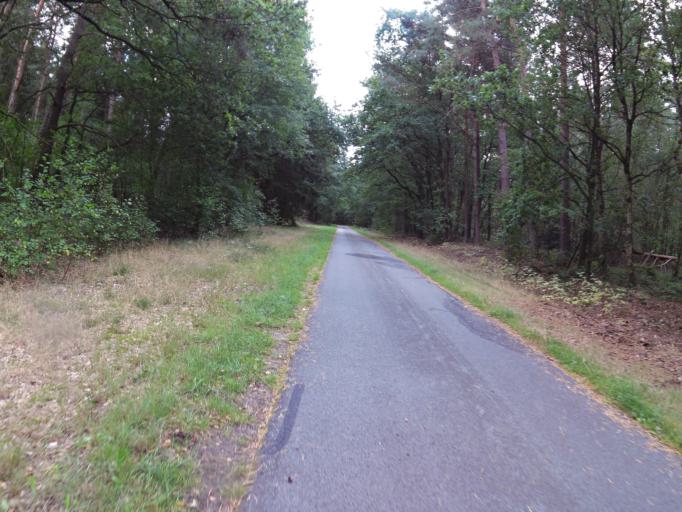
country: DE
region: Lower Saxony
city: Selsingen
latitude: 53.3638
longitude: 9.1670
